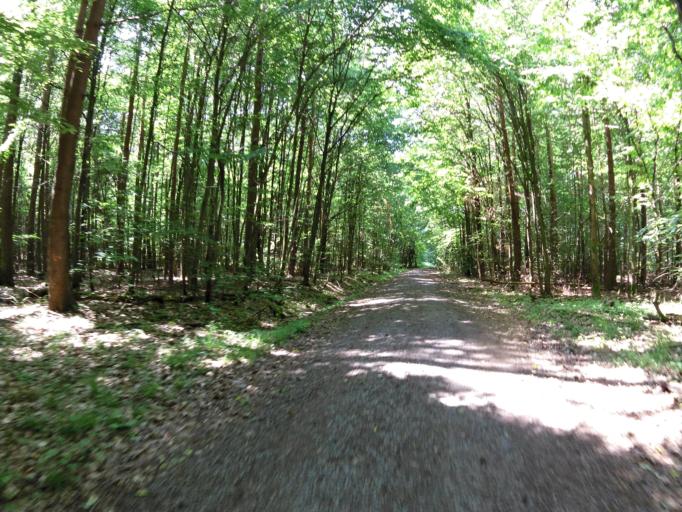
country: DE
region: Bavaria
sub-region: Regierungsbezirk Unterfranken
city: Kist
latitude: 49.7283
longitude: 9.8590
